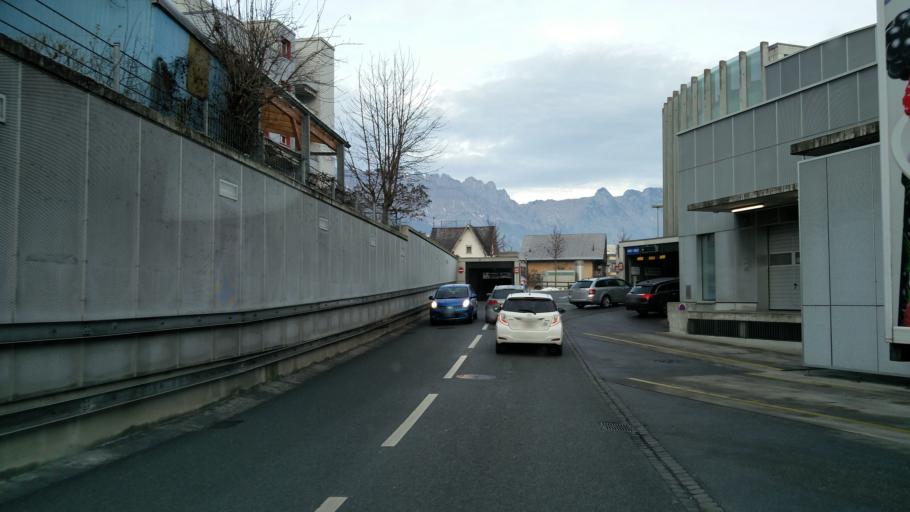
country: CH
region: Saint Gallen
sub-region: Wahlkreis Werdenberg
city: Buchs
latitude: 47.1637
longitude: 9.4719
